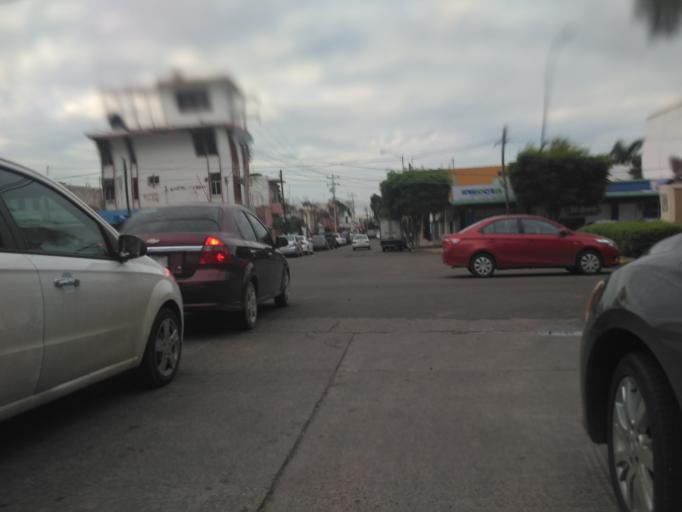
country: MX
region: Sinaloa
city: Culiacan
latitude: 24.8014
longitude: -107.3976
